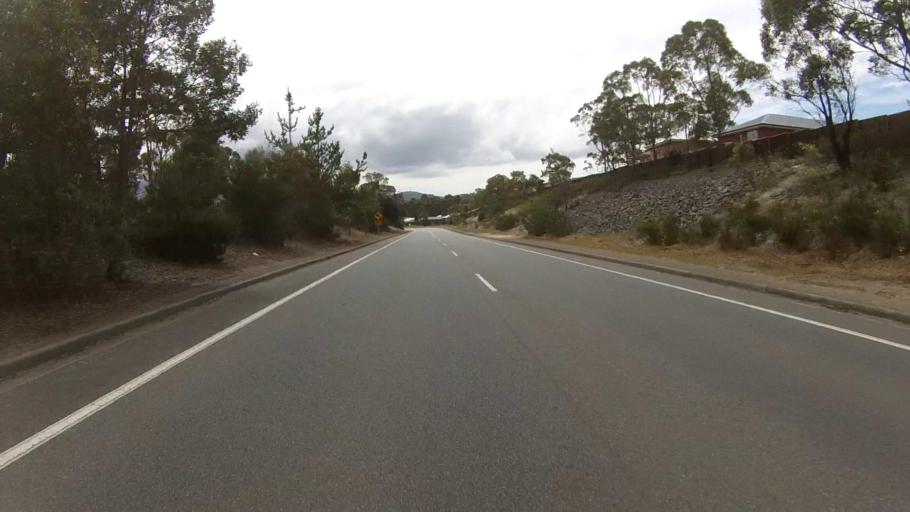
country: AU
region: Tasmania
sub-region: Kingborough
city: Kingston
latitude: -42.9919
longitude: 147.2943
